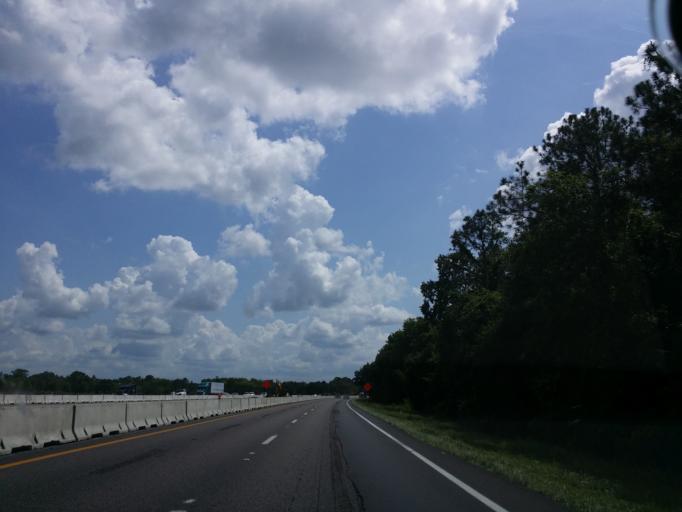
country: US
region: Florida
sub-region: Pasco County
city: Wesley Chapel
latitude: 28.2985
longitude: -82.3247
